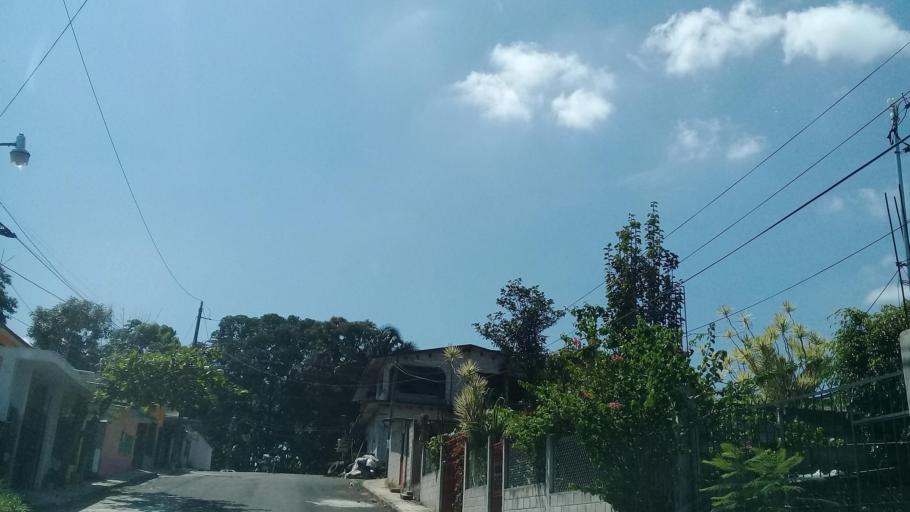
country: MX
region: Veracruz
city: Amatlan de los Reyes
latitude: 18.8410
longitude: -96.9113
